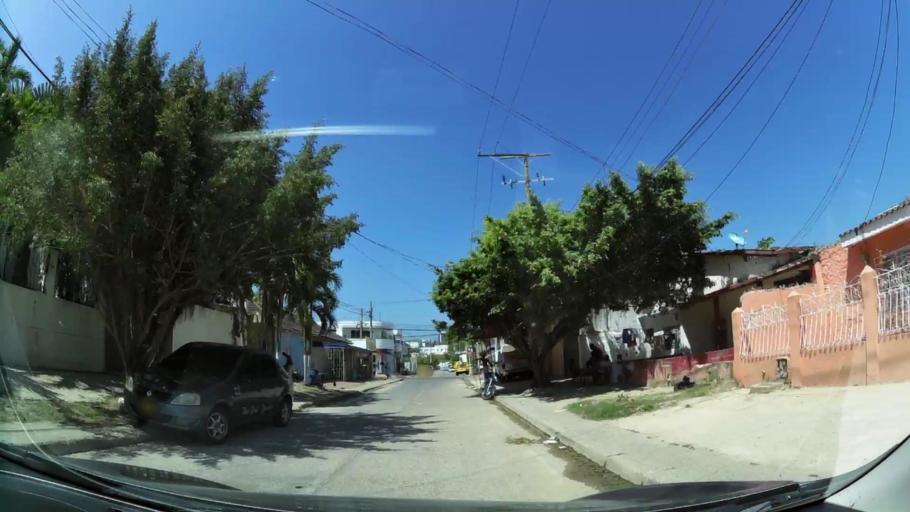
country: CO
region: Bolivar
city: Cartagena
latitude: 10.4301
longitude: -75.5330
